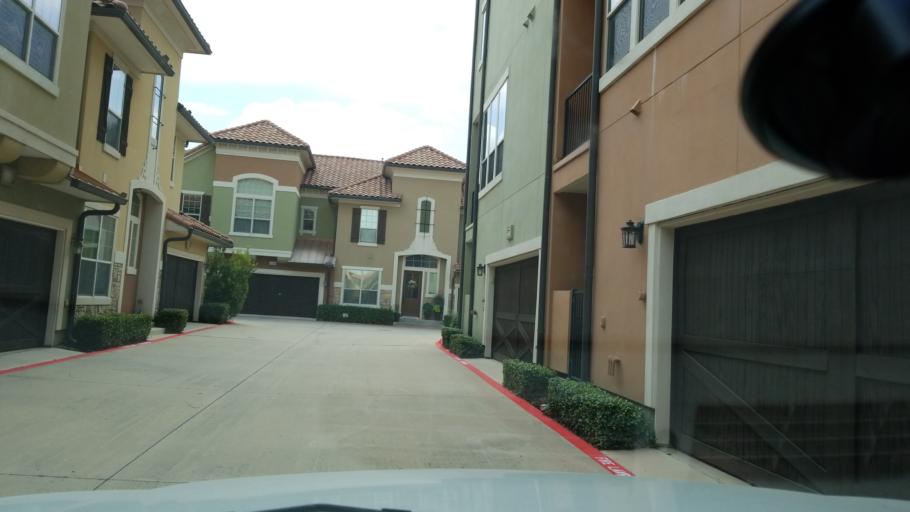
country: US
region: Texas
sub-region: Dallas County
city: Farmers Branch
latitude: 32.9013
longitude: -96.9345
